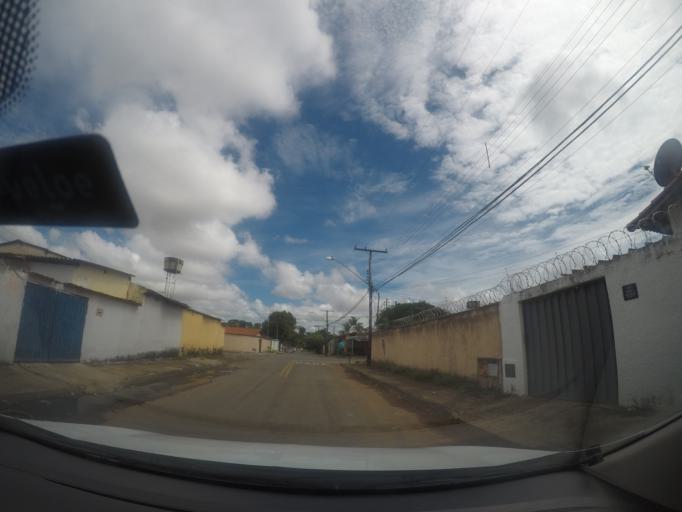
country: BR
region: Goias
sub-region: Goiania
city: Goiania
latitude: -16.6575
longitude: -49.3032
